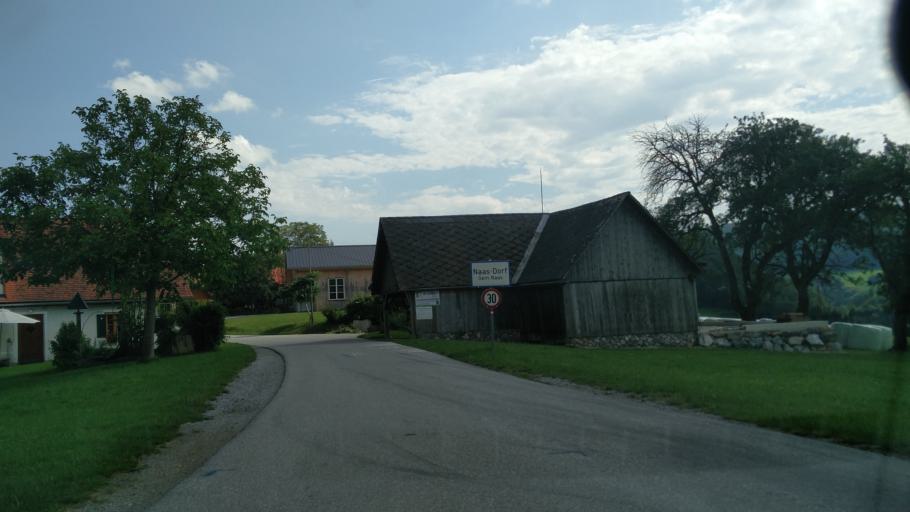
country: AT
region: Styria
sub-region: Politischer Bezirk Weiz
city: Naas
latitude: 47.2482
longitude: 15.6040
